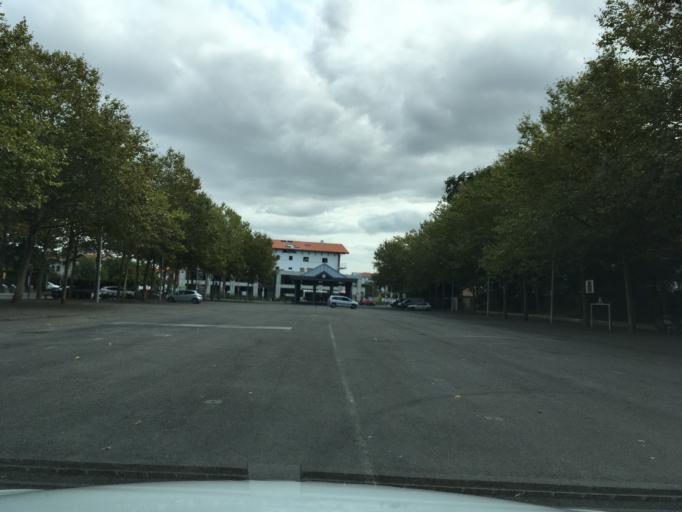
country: FR
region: Aquitaine
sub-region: Departement des Pyrenees-Atlantiques
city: Anglet
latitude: 43.4838
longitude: -1.5129
